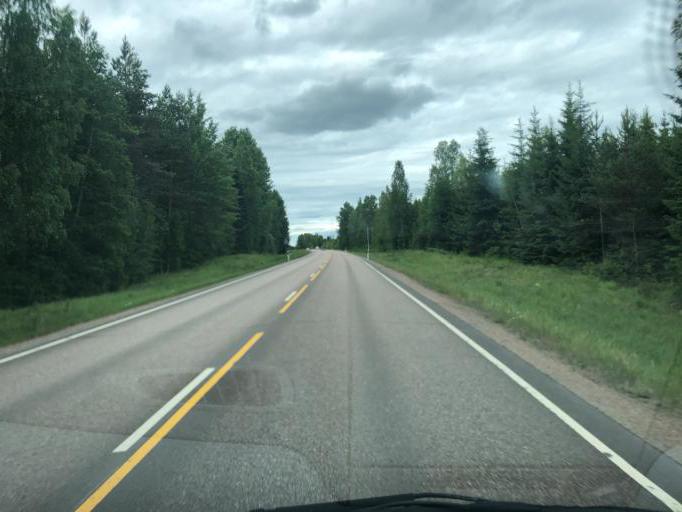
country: FI
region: Southern Savonia
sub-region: Mikkeli
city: Maentyharju
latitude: 61.1265
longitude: 27.1026
